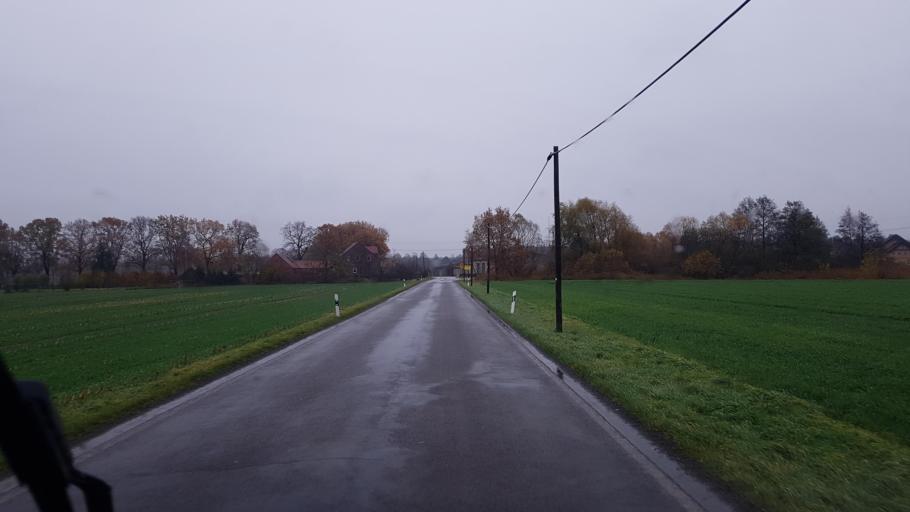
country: DE
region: Brandenburg
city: Altdobern
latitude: 51.6616
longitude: 14.0109
